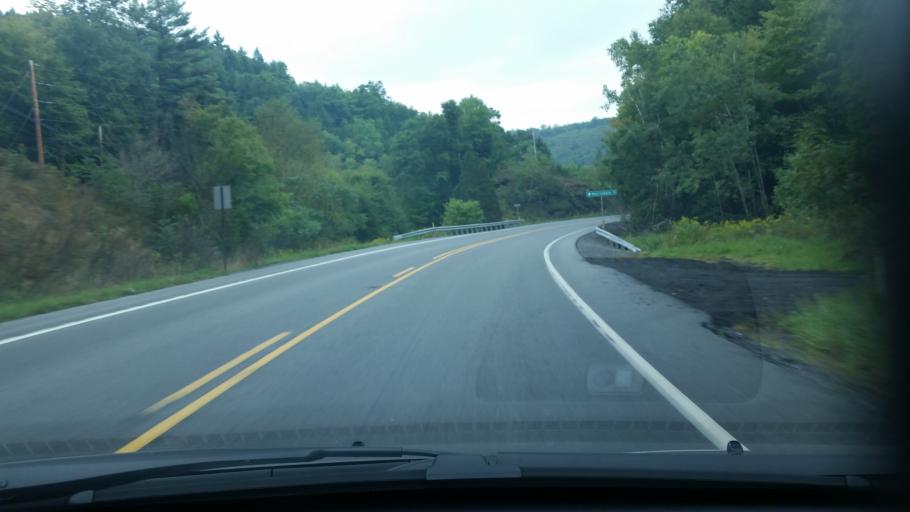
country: US
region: Pennsylvania
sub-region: Clearfield County
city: Shiloh
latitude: 41.0890
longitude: -78.2450
